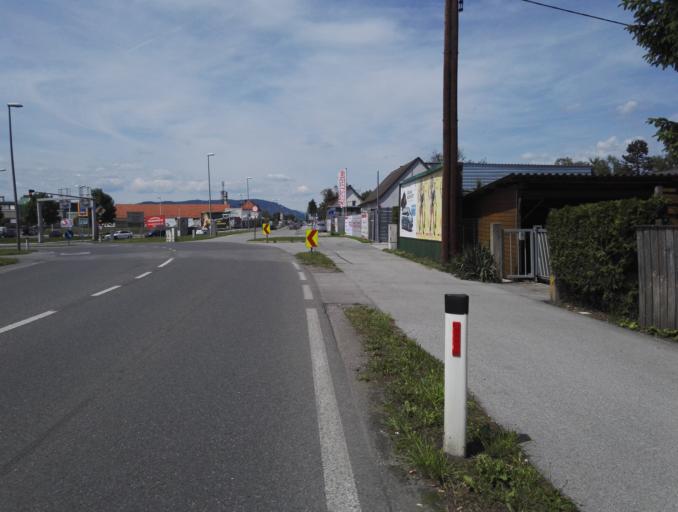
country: AT
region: Styria
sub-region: Politischer Bezirk Graz-Umgebung
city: Feldkirchen bei Graz
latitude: 47.0169
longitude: 15.4402
